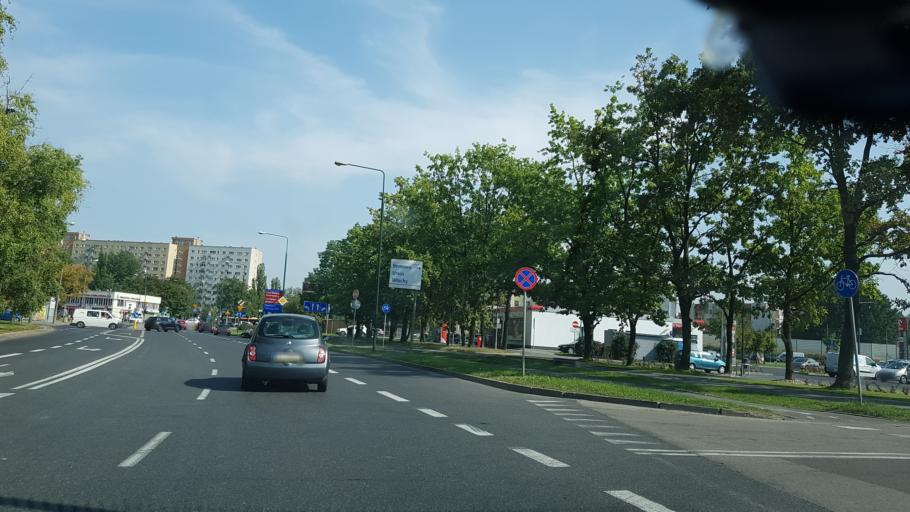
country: PL
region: Masovian Voivodeship
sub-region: Warszawa
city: Bielany
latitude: 52.2708
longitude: 20.9314
